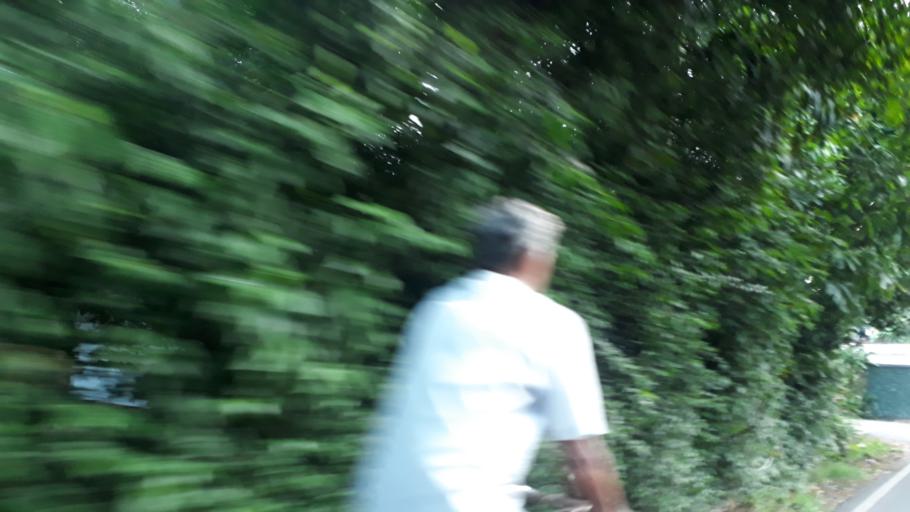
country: LK
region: Western
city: Gampaha
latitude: 7.1013
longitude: 79.9835
